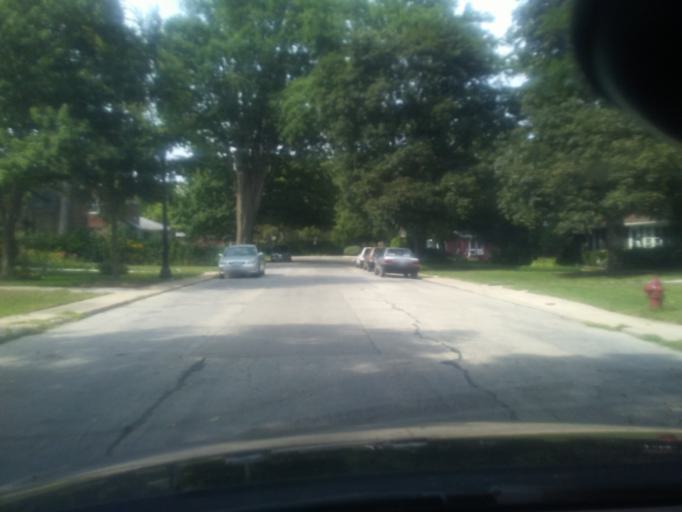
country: US
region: Illinois
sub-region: Cook County
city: Evanston
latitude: 42.0328
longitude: -87.7025
